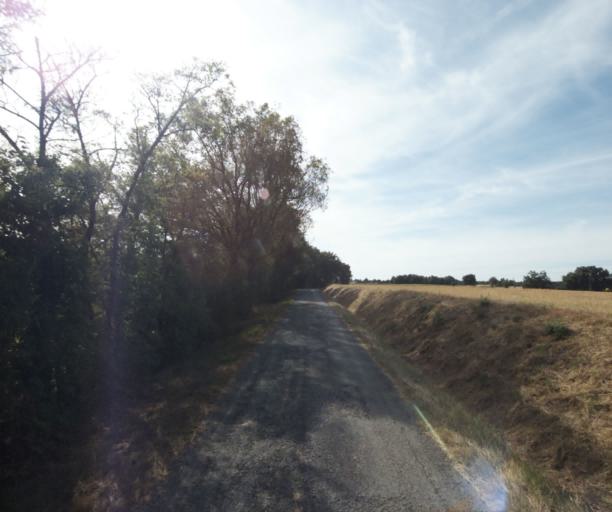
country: FR
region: Midi-Pyrenees
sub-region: Departement du Tarn
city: Soual
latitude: 43.5312
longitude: 2.0709
